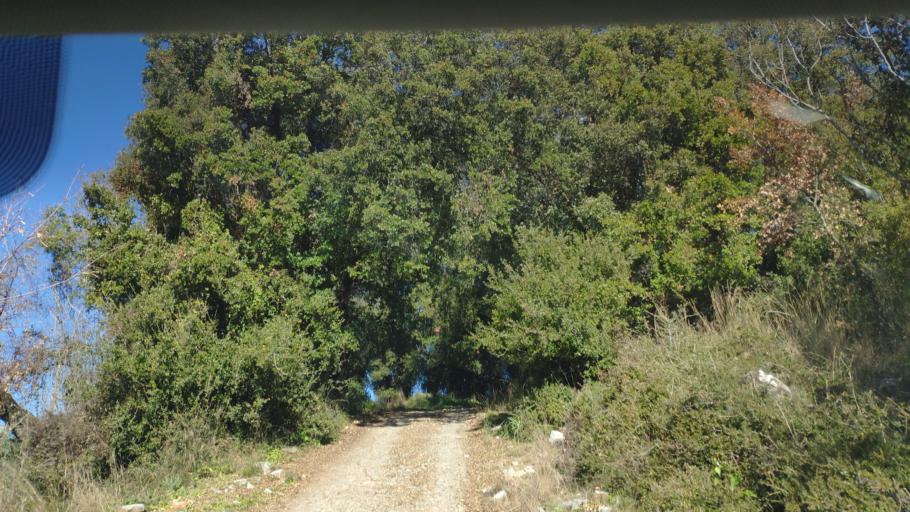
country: GR
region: West Greece
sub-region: Nomos Aitolias kai Akarnanias
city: Thermo
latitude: 38.5821
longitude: 21.6309
